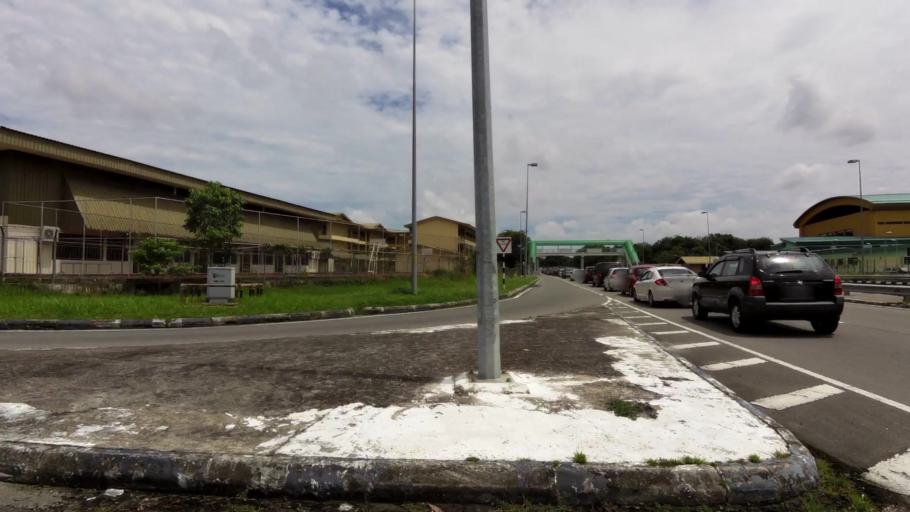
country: BN
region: Brunei and Muara
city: Bandar Seri Begawan
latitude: 4.9457
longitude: 114.9417
